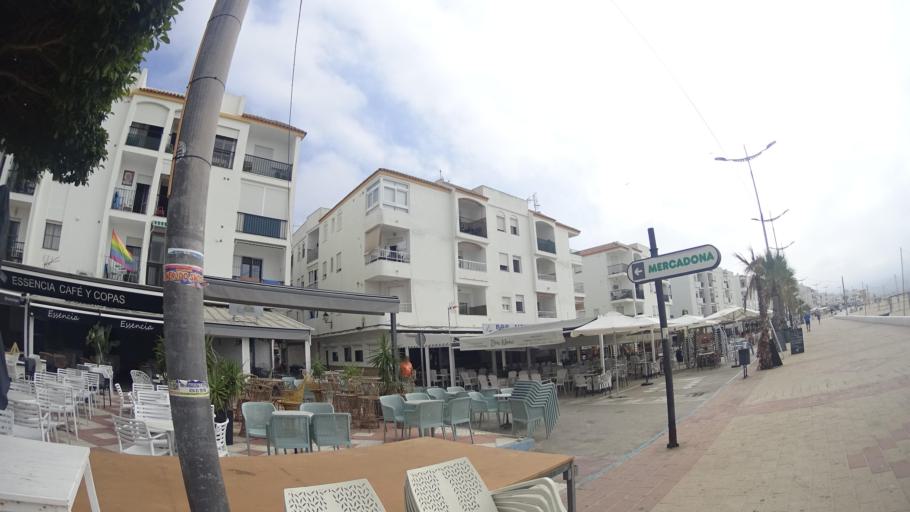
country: ES
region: Andalusia
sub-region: Provincia de Cadiz
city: Barbate de Franco
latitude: 36.1869
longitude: -5.9203
